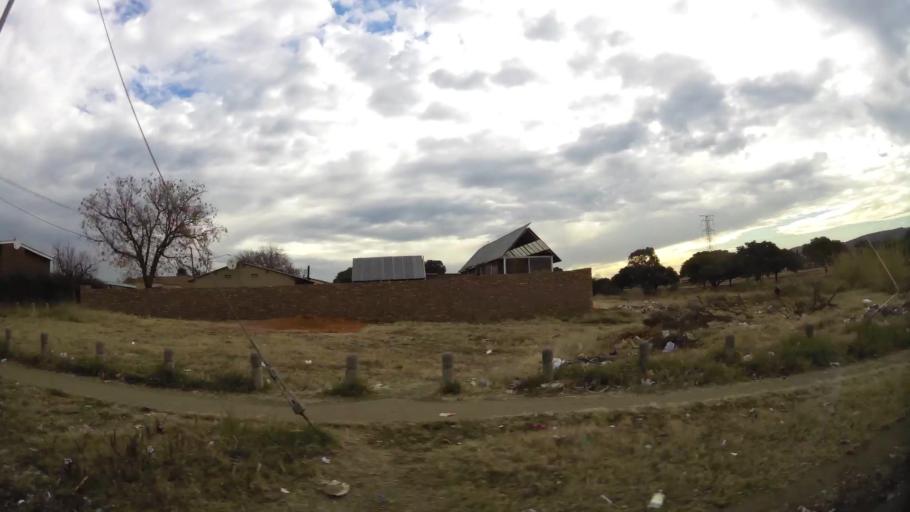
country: ZA
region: Gauteng
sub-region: City of Tshwane Metropolitan Municipality
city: Pretoria
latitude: -25.7115
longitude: 28.3143
